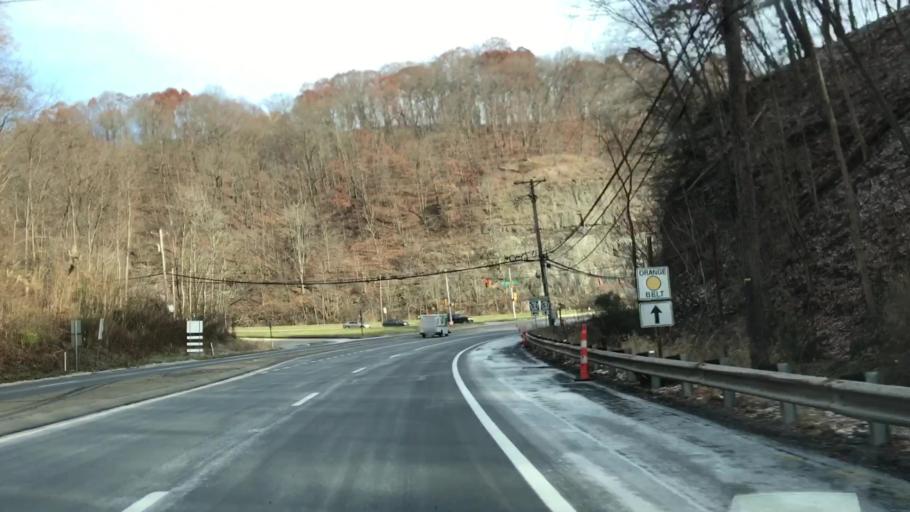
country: US
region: Pennsylvania
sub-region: Allegheny County
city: Edgeworth
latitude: 40.5372
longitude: -80.2011
